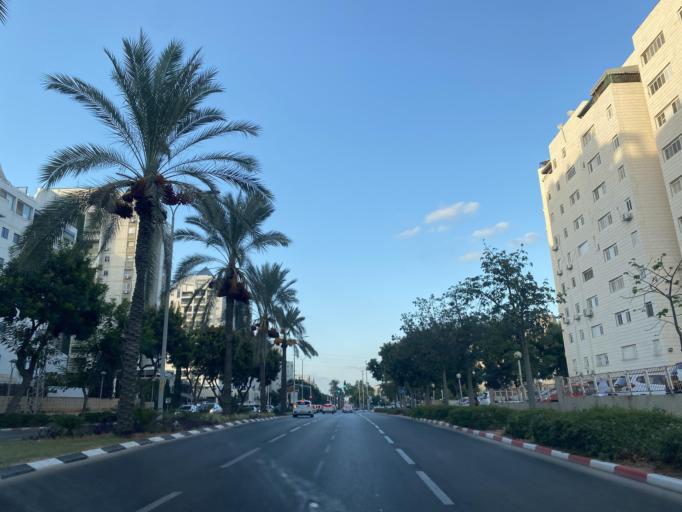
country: IL
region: Southern District
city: Ashdod
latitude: 31.7853
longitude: 34.6457
